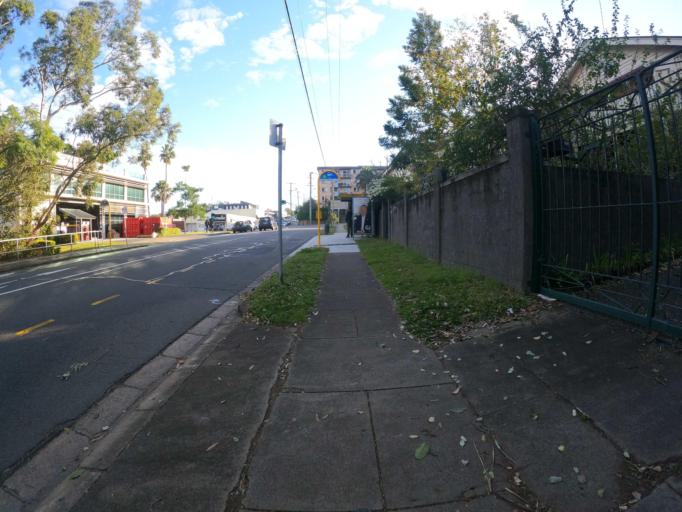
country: AU
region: Queensland
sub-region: Brisbane
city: Windsor
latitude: -27.4381
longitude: 153.0271
